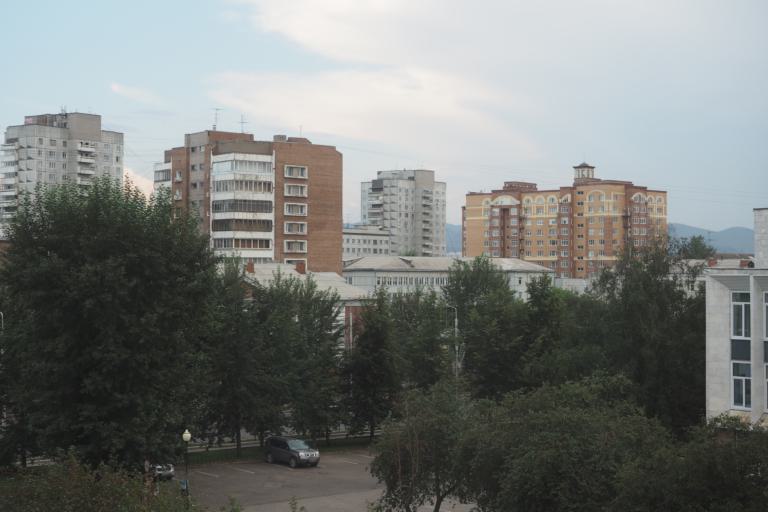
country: RU
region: Krasnoyarskiy
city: Krasnoyarsk
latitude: 56.0121
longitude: 92.8880
